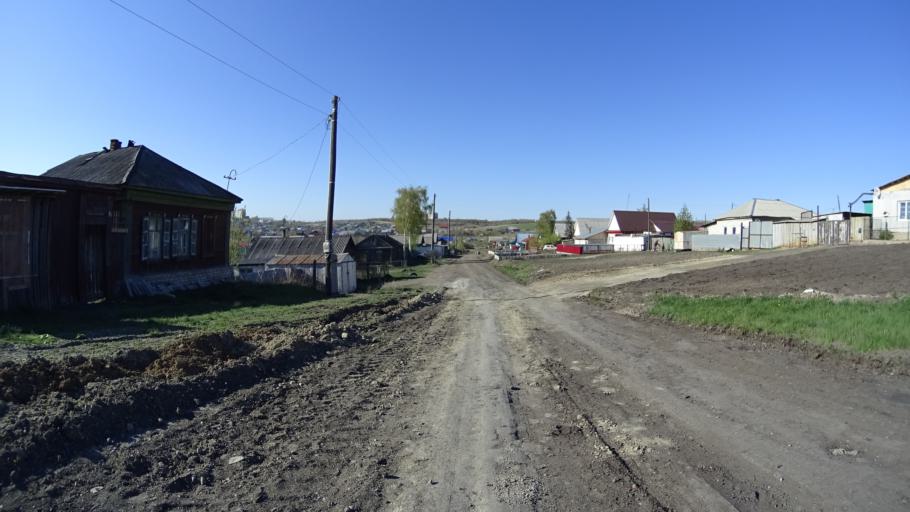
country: RU
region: Chelyabinsk
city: Troitsk
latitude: 54.0903
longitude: 61.6000
